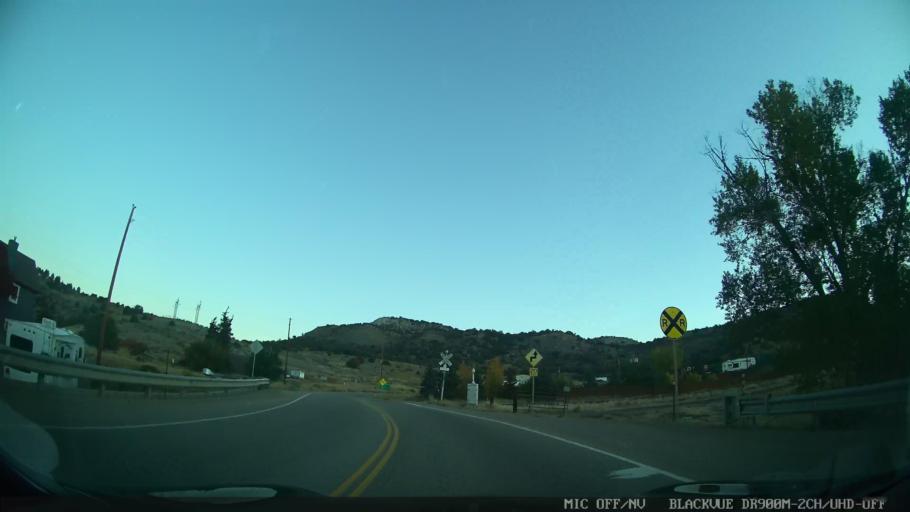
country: US
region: Colorado
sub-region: Eagle County
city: Edwards
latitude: 39.7018
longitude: -106.6780
